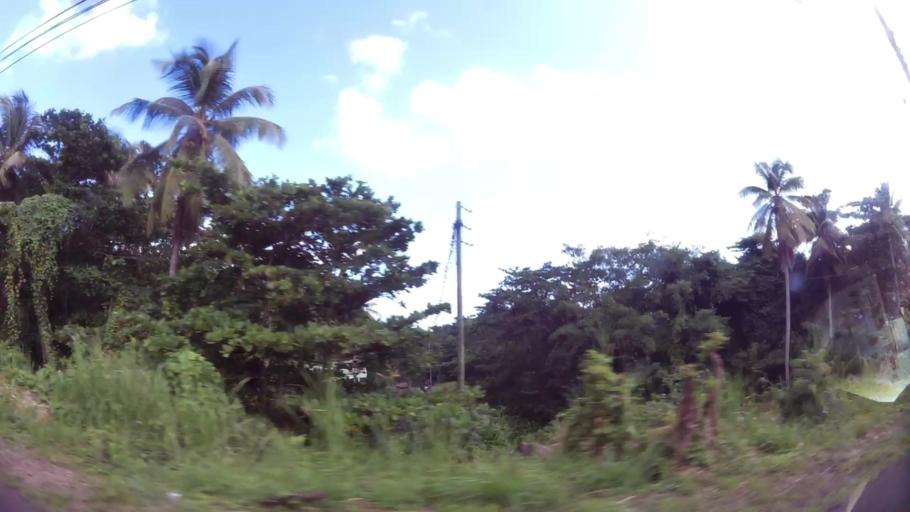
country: DM
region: Saint Andrew
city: Marigot
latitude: 15.5276
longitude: -61.2744
